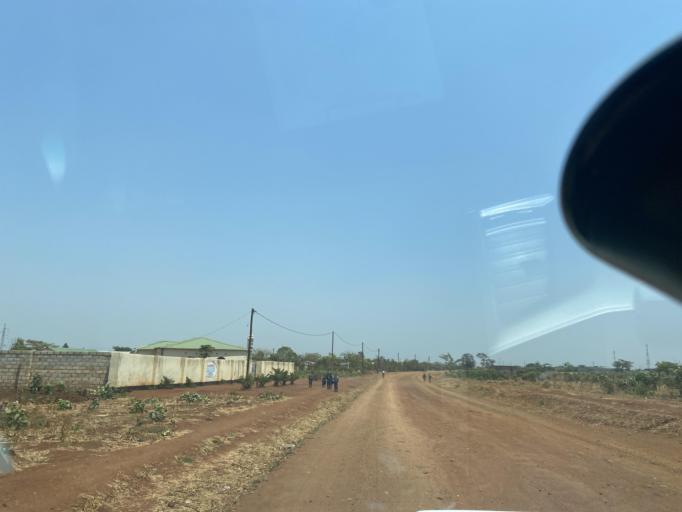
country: ZM
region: Lusaka
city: Kafue
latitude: -15.5168
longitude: 27.9364
